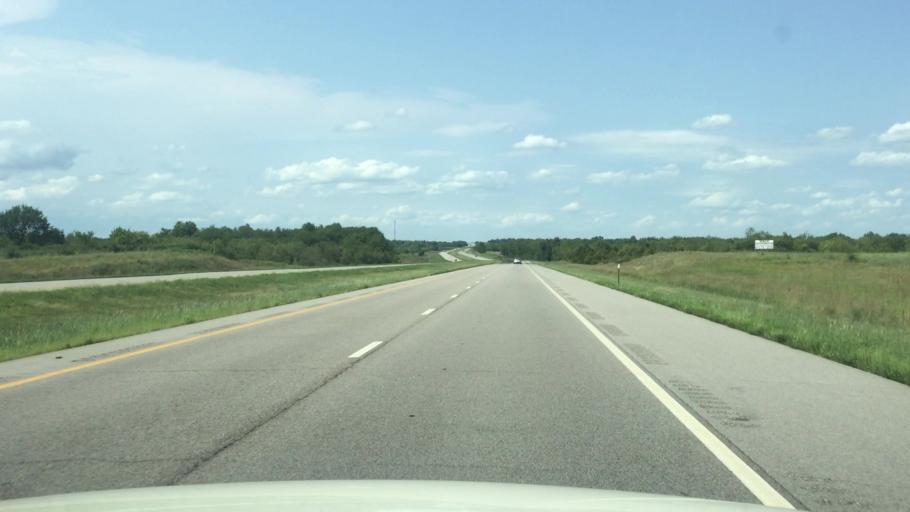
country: US
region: Kansas
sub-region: Linn County
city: La Cygne
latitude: 38.4455
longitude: -94.6861
